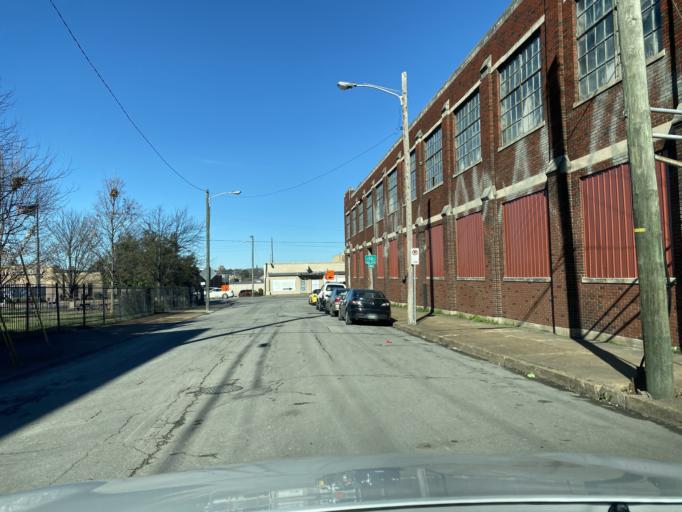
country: US
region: Tennessee
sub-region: Davidson County
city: Nashville
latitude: 36.1560
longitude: -86.7941
